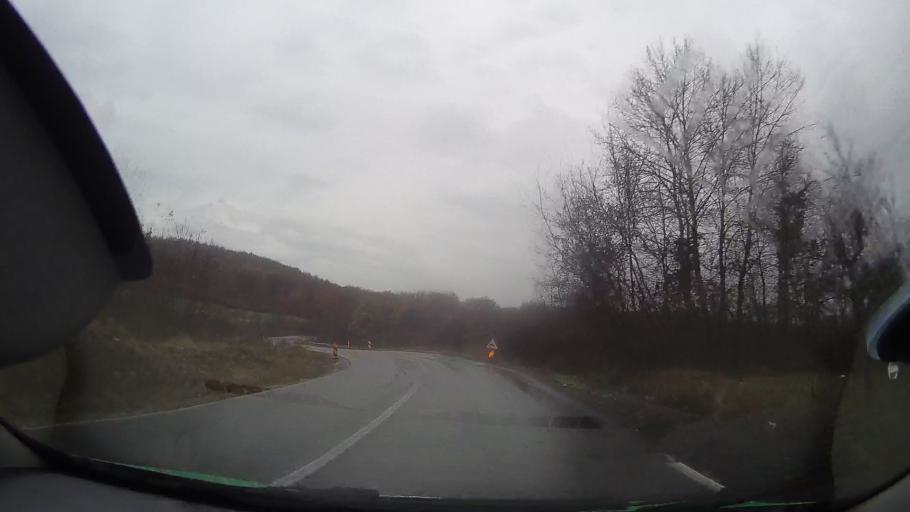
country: RO
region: Bihor
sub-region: Comuna Rabagani
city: Rabagani
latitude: 46.7316
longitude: 22.2320
